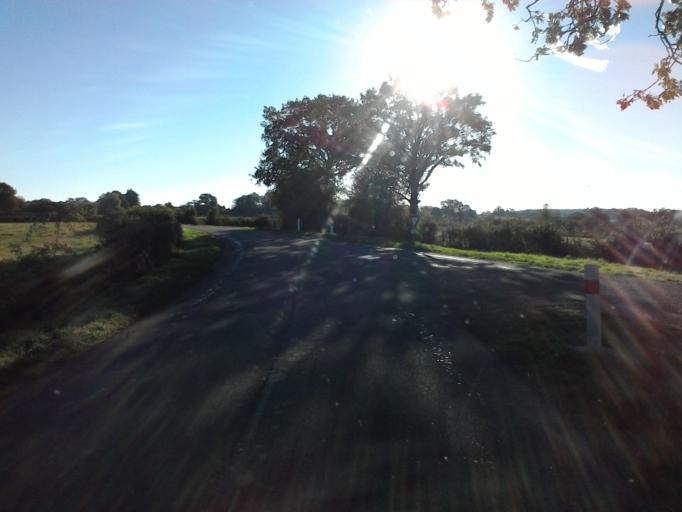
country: FR
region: Bourgogne
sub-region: Departement de la Cote-d'Or
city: Saulieu
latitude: 47.2762
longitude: 4.2036
